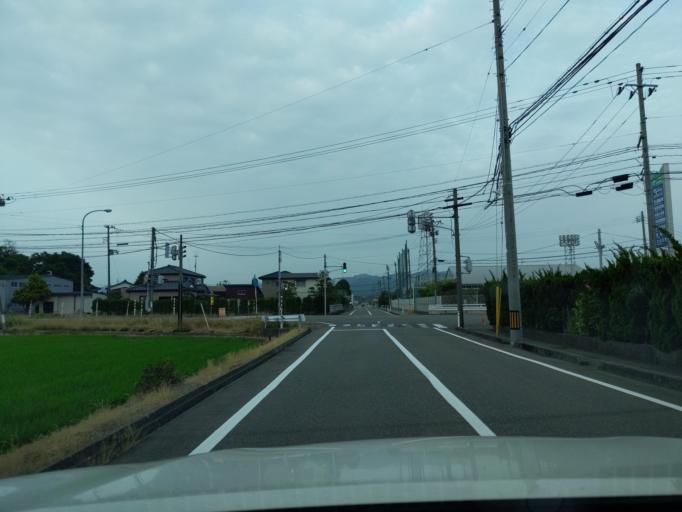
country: JP
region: Niigata
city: Kashiwazaki
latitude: 37.4229
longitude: 138.6190
